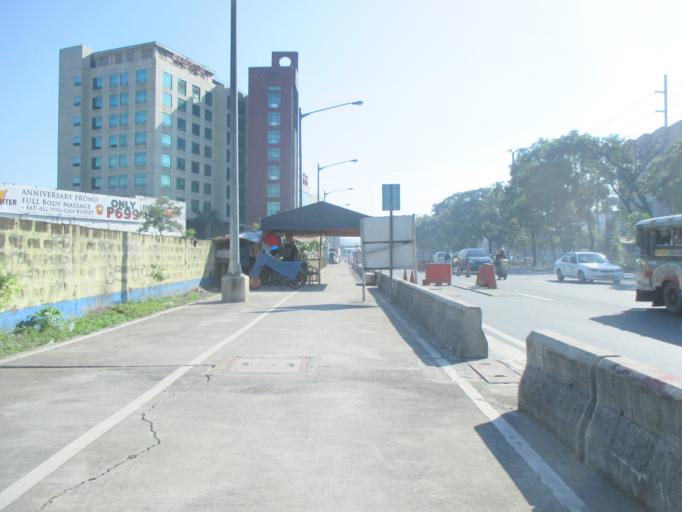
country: PH
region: Metro Manila
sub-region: Marikina
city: Calumpang
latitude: 14.6194
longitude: 121.0947
